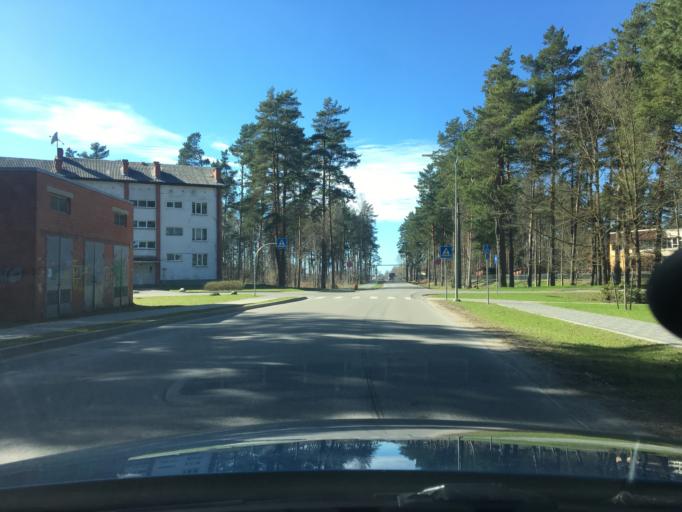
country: LV
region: Salaspils
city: Salaspils
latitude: 56.8707
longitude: 24.3444
